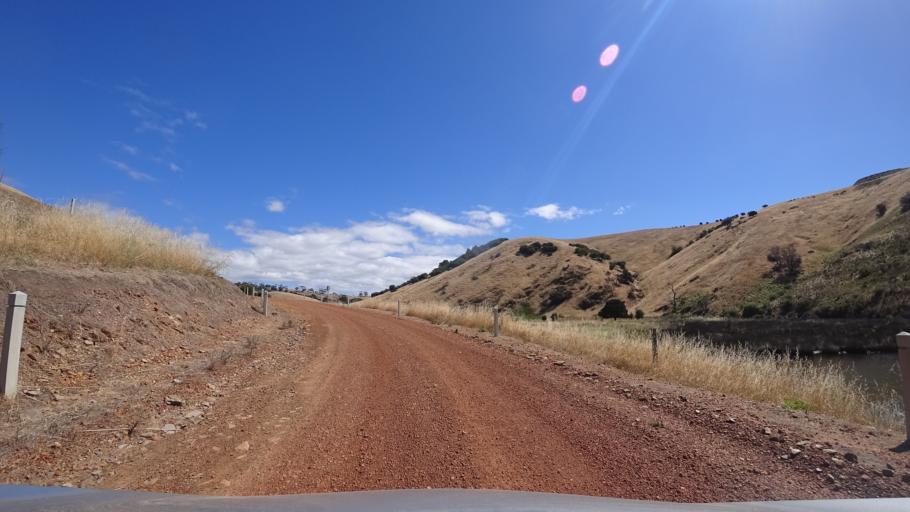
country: AU
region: South Australia
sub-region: Kangaroo Island
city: Kingscote
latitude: -35.6778
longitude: 136.9716
